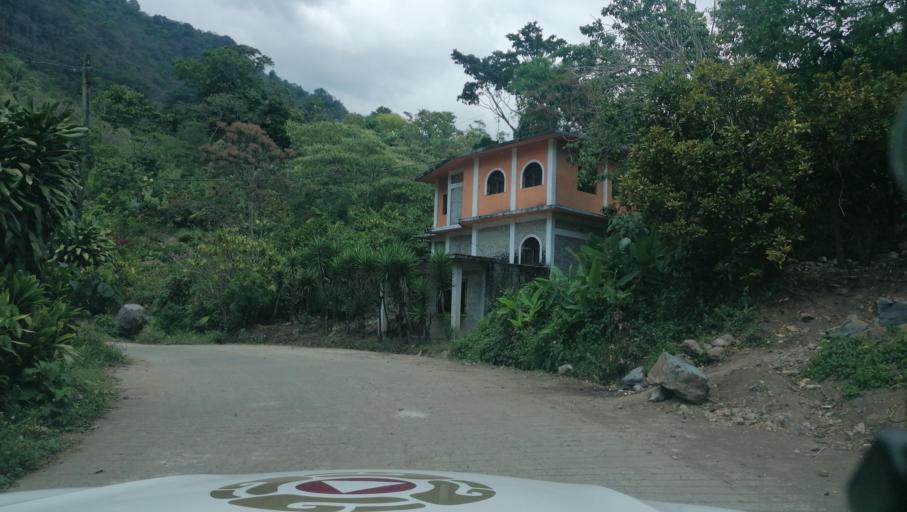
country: MX
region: Chiapas
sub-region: Cacahoatan
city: Benito Juarez
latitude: 15.1099
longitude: -92.2092
